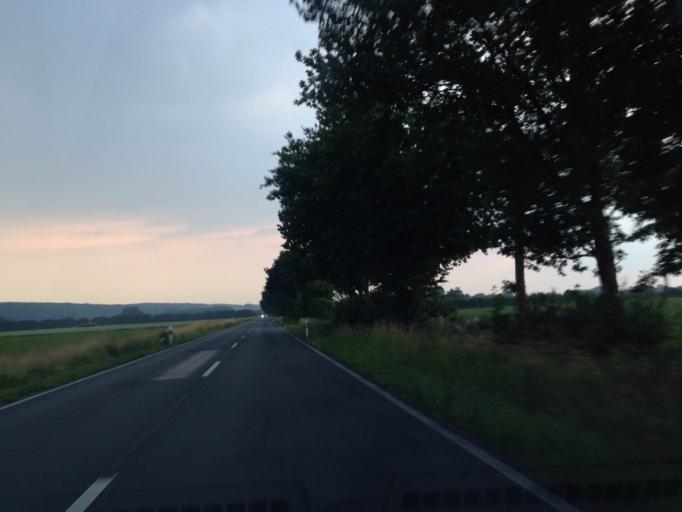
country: DE
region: North Rhine-Westphalia
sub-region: Regierungsbezirk Munster
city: Havixbeck
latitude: 51.9672
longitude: 7.4494
